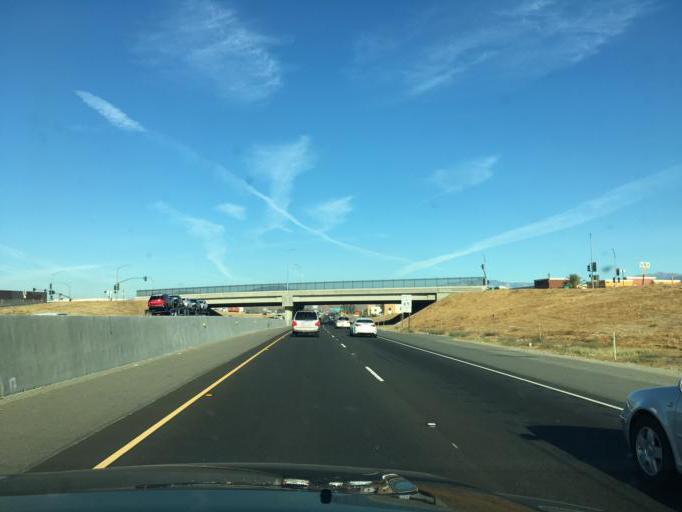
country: US
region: California
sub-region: Los Angeles County
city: Pomona
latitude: 34.0524
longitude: -117.7801
